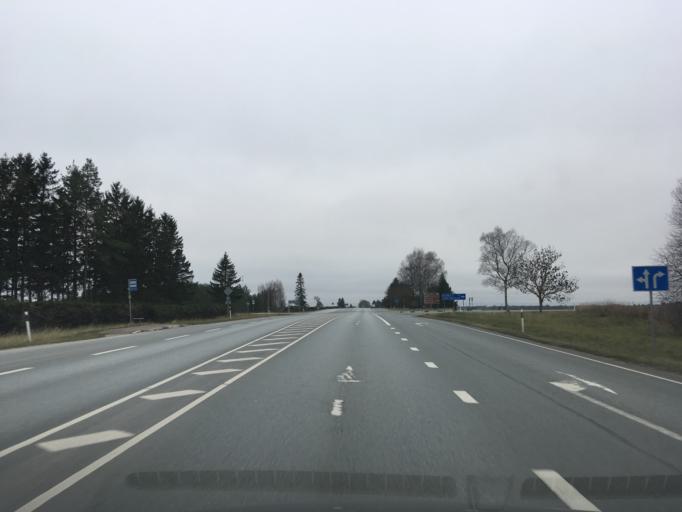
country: EE
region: Ida-Virumaa
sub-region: Aseri vald
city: Aseri
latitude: 59.4306
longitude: 26.6993
